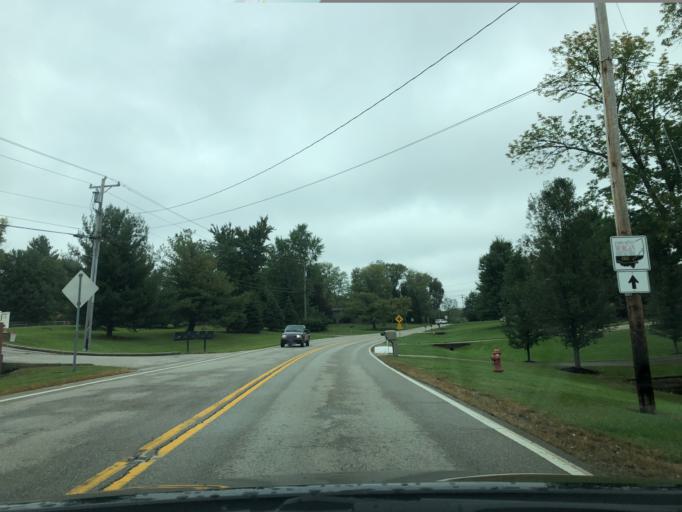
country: US
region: Ohio
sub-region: Hamilton County
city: The Village of Indian Hill
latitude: 39.2282
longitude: -84.2769
